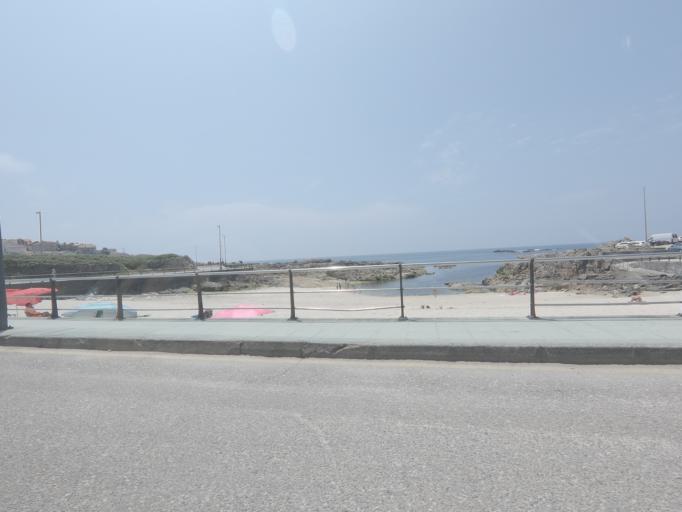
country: ES
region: Galicia
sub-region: Provincia de Pontevedra
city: A Guarda
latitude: 41.9103
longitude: -8.8761
